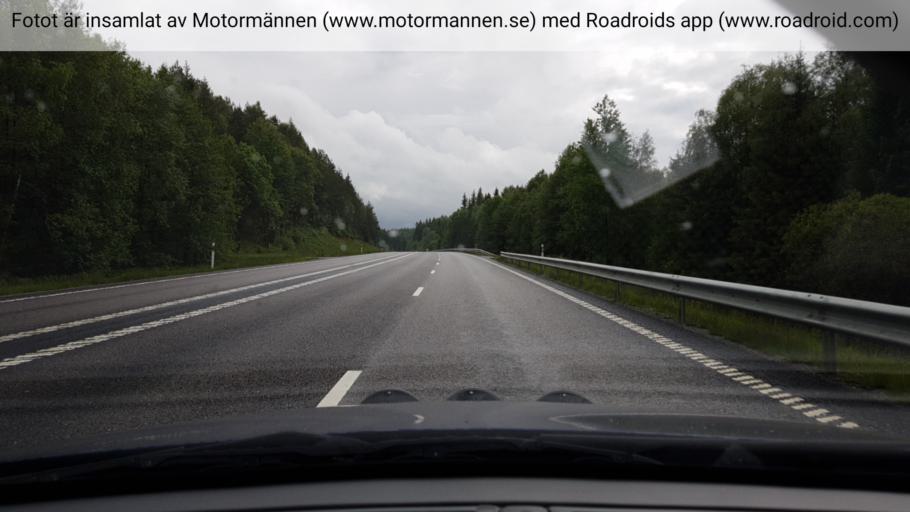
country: SE
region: Vaestra Goetaland
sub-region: Boras Kommun
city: Viskafors
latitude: 57.6225
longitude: 12.8854
